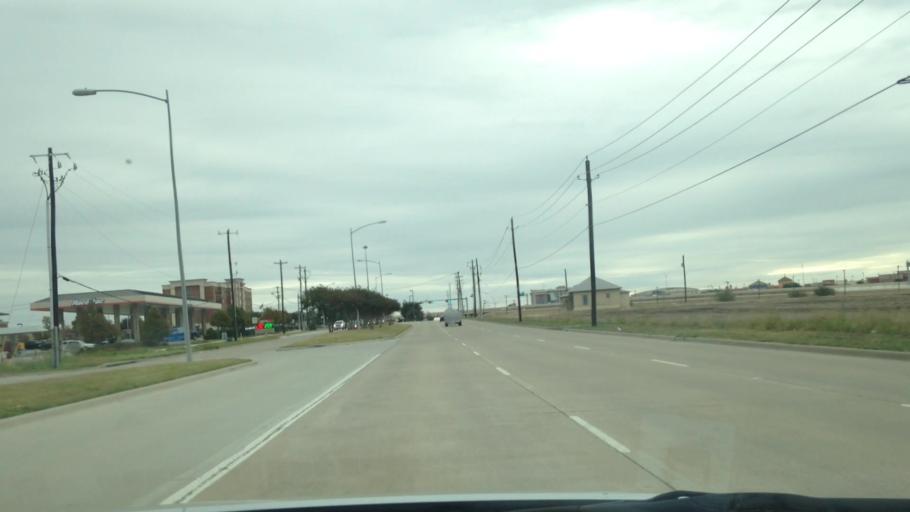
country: US
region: Texas
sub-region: Collin County
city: Allen
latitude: 33.1298
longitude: -96.6662
